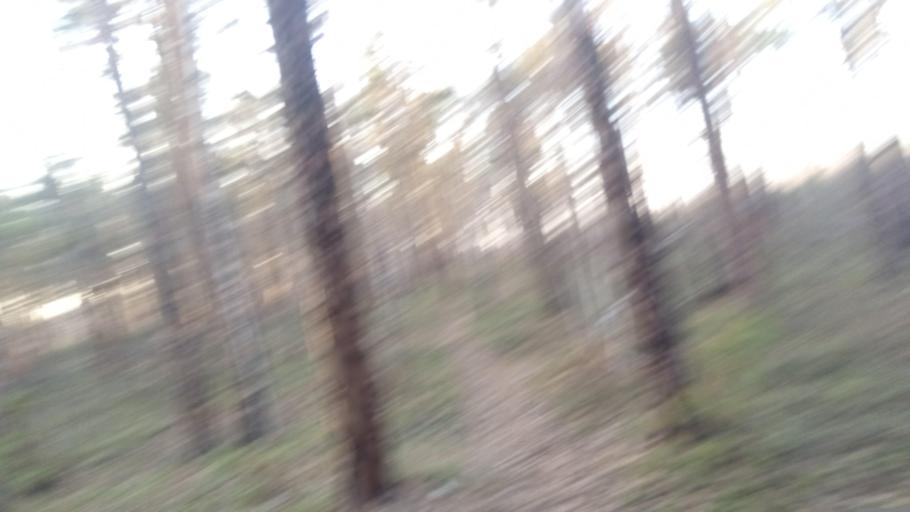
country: RU
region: Chelyabinsk
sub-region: Gorod Chelyabinsk
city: Chelyabinsk
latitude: 55.1601
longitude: 61.3238
